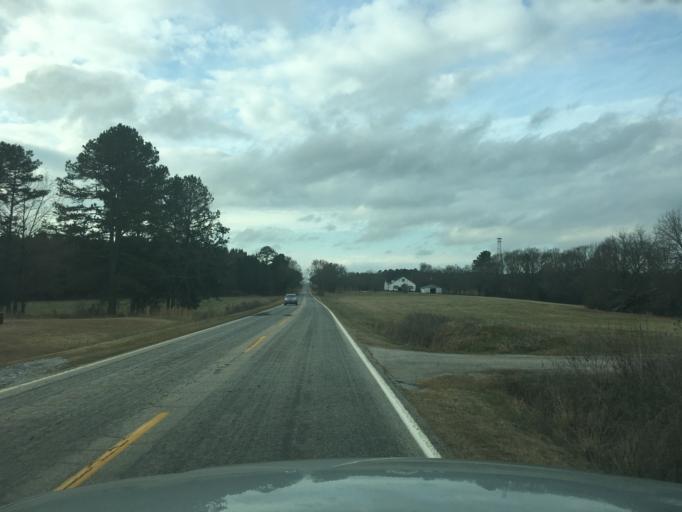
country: US
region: South Carolina
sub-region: Abbeville County
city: Due West
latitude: 34.3220
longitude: -82.4687
